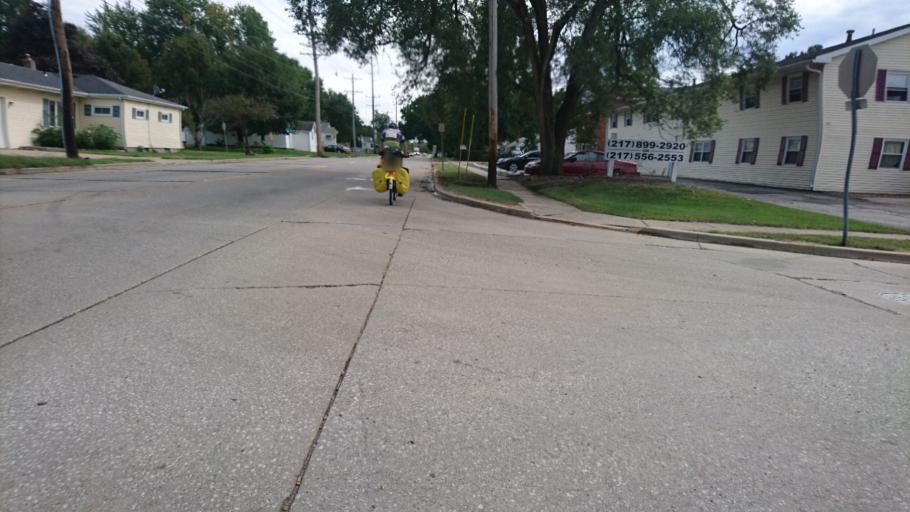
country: US
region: Illinois
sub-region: Sangamon County
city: Southern View
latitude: 39.7756
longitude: -89.6544
